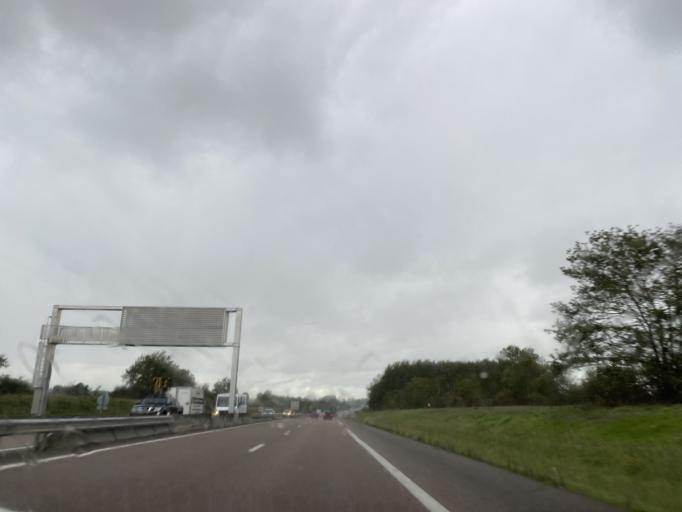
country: FR
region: Auvergne
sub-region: Departement de l'Allier
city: Estivareilles
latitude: 46.4133
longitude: 2.7057
